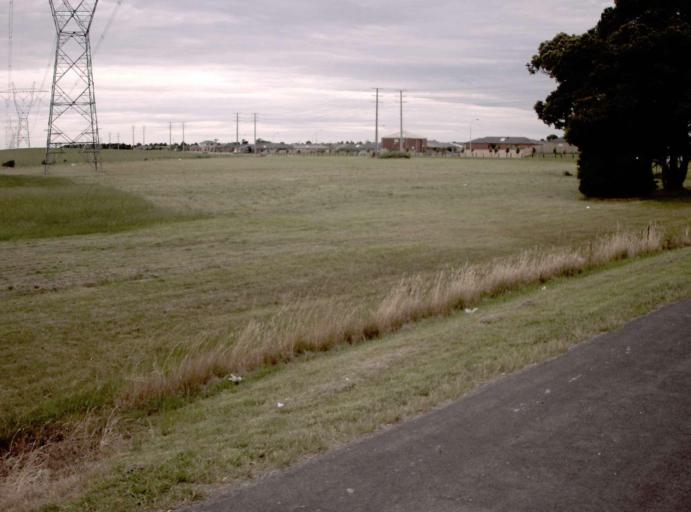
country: AU
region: Victoria
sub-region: Casey
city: Cranbourne North
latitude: -38.0892
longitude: 145.2796
